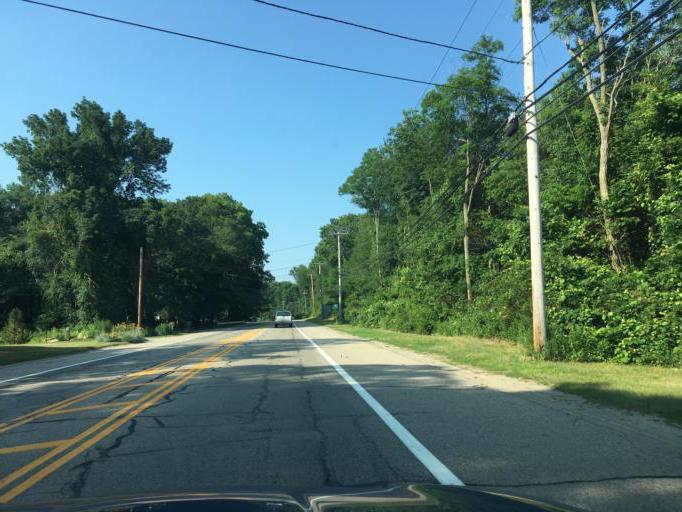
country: US
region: Rhode Island
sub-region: Washington County
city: Exeter
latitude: 41.5262
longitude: -71.5517
